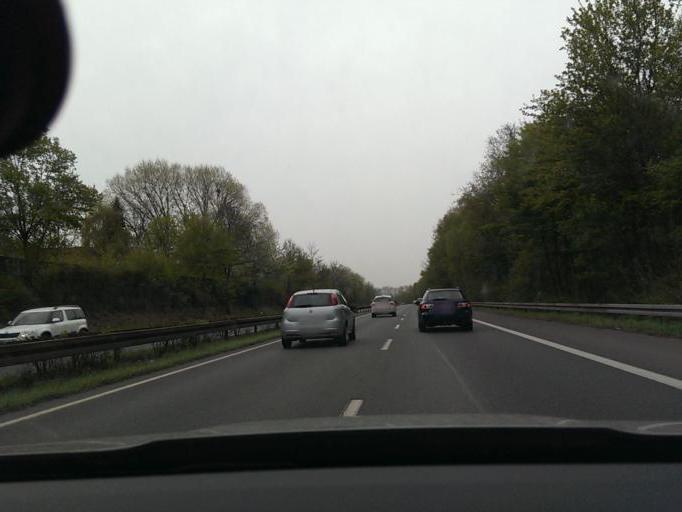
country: DE
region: Lower Saxony
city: Auf der Horst
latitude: 52.4035
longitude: 9.6598
